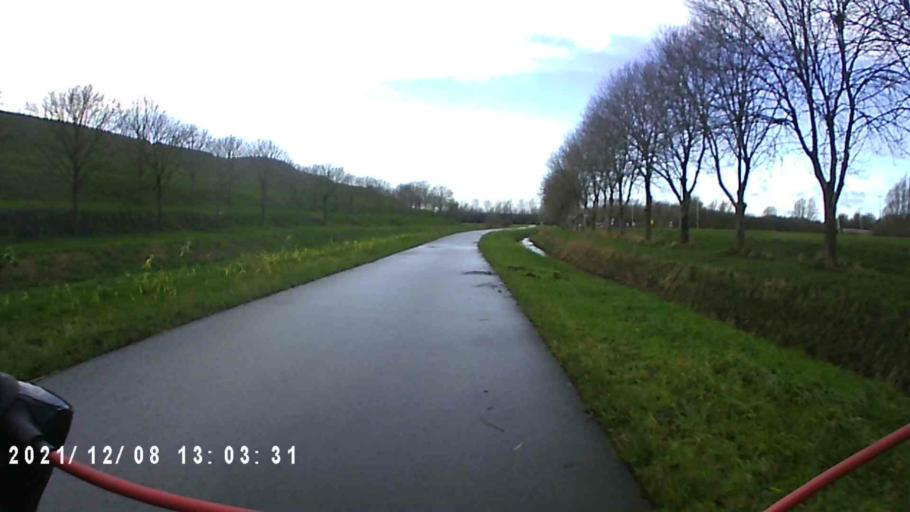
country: NL
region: Groningen
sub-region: Gemeente Haren
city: Haren
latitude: 53.2041
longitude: 6.6197
